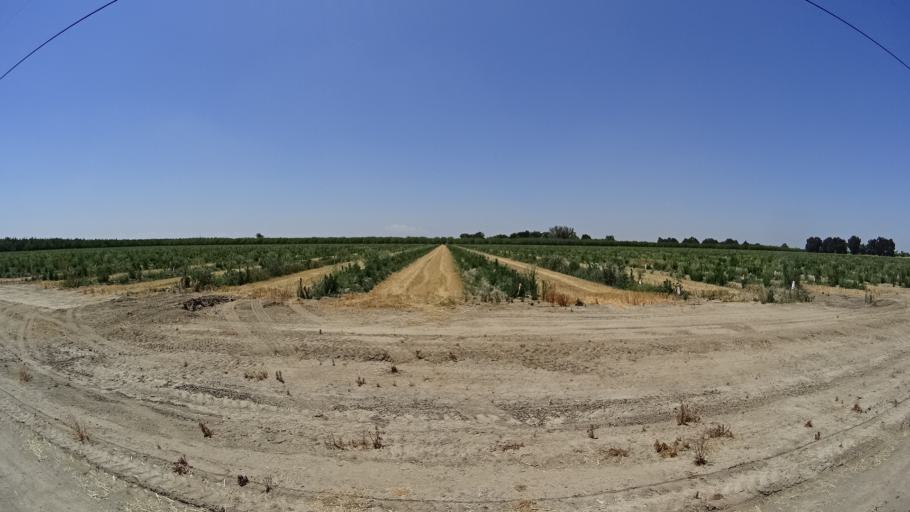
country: US
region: California
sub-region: Kings County
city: Lucerne
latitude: 36.4188
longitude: -119.6189
